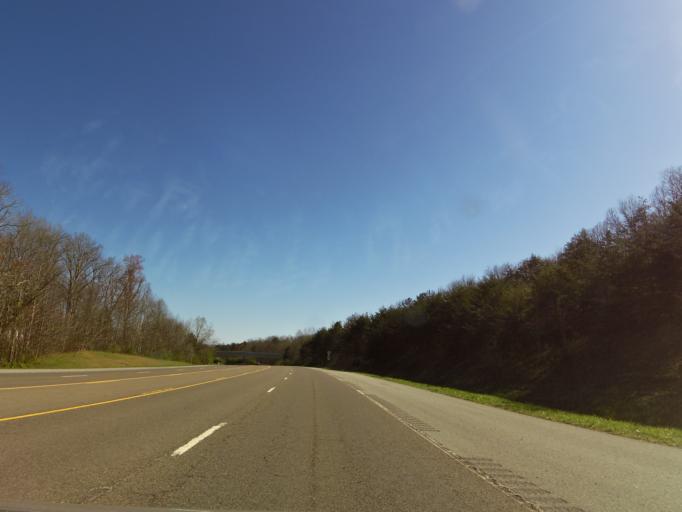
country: US
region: Tennessee
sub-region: Scott County
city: Oneida
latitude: 36.4619
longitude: -84.5483
